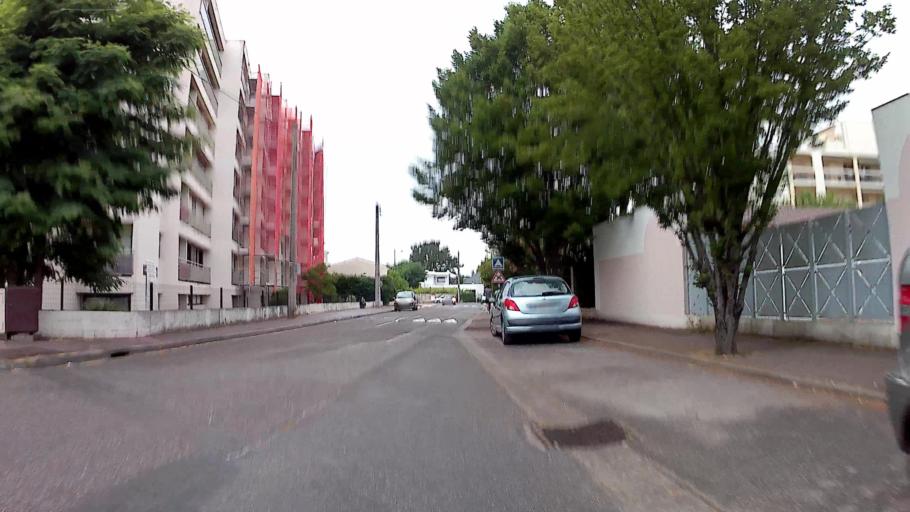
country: FR
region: Aquitaine
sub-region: Departement de la Gironde
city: Le Bouscat
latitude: 44.8596
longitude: -0.6042
